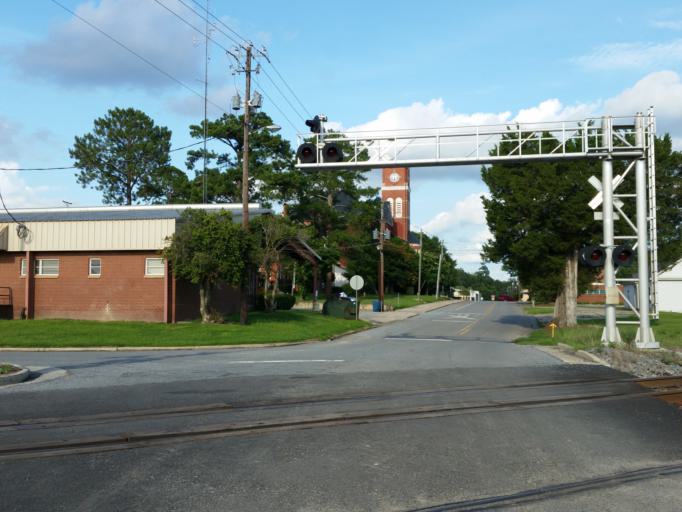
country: US
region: Georgia
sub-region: Dooly County
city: Vienna
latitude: 32.0910
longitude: -83.7990
